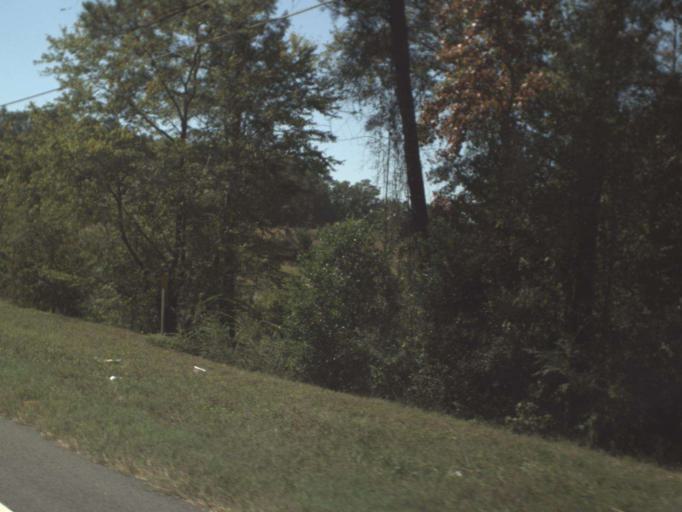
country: US
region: Alabama
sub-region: Covington County
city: Florala
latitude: 30.9731
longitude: -86.3533
